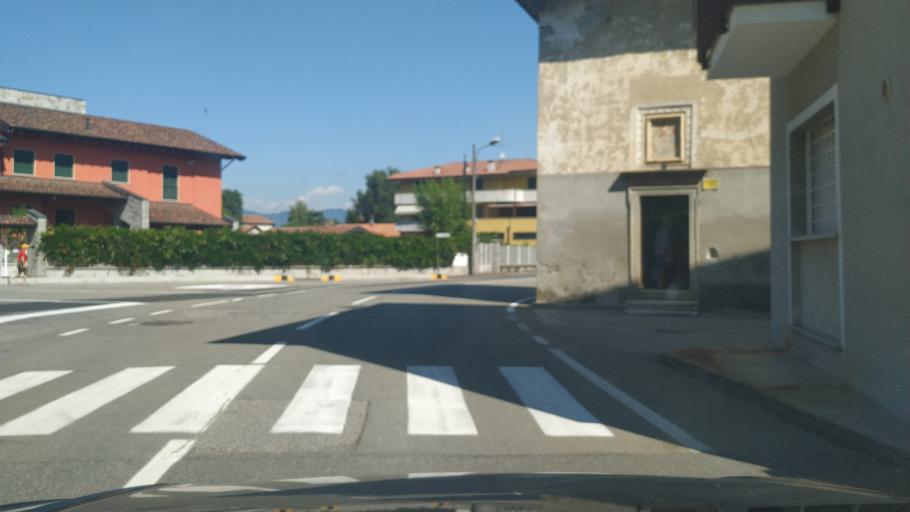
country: IT
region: Piedmont
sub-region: Provincia di Novara
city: Borgomanero
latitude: 45.7022
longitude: 8.4651
